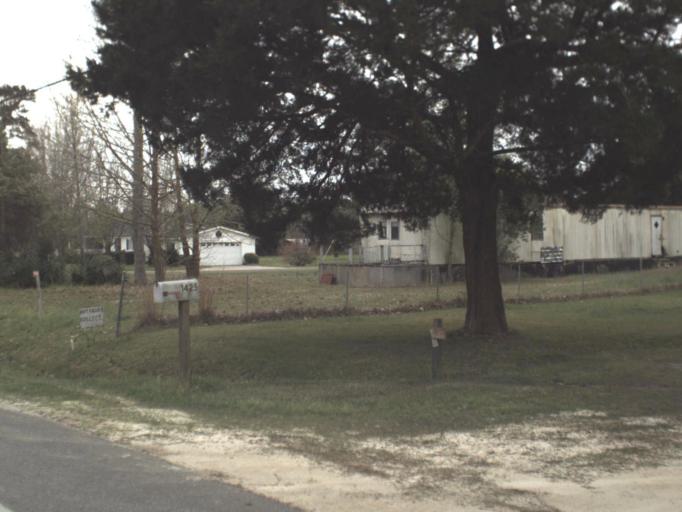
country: US
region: Florida
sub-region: Gulf County
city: Wewahitchka
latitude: 30.0980
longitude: -85.1991
